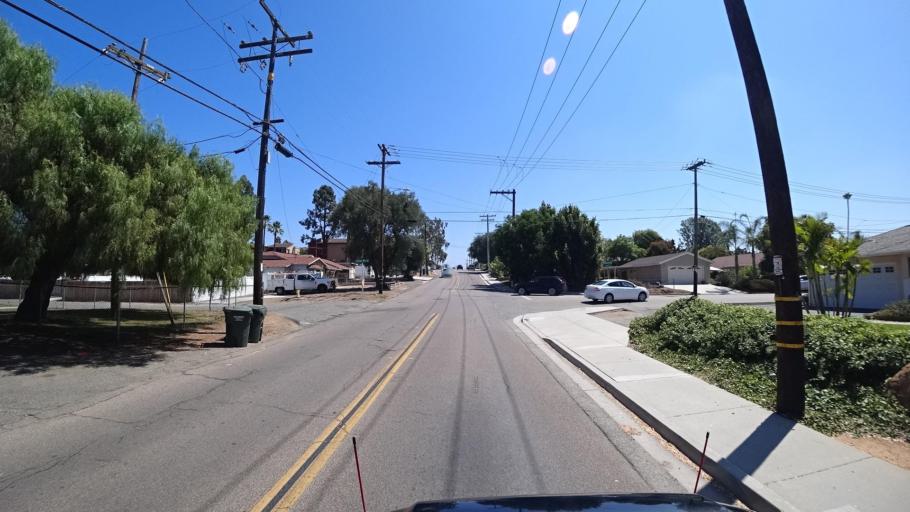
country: US
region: California
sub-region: San Diego County
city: Fallbrook
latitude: 33.3820
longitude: -117.2431
